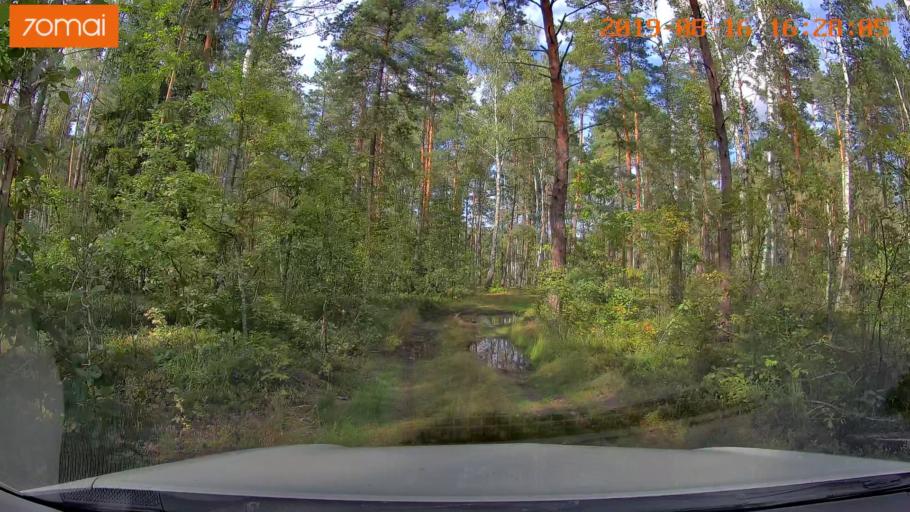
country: BY
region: Mogilev
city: Asipovichy
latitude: 53.2240
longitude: 28.7703
